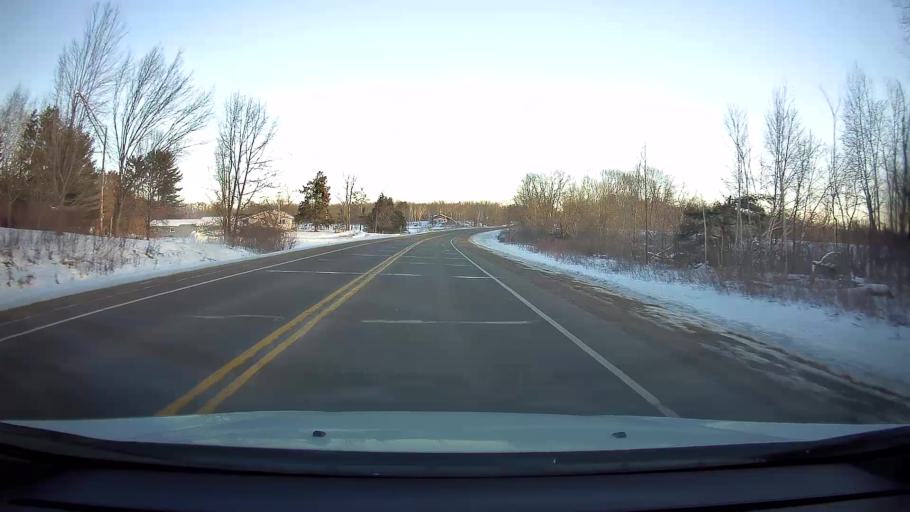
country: US
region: Wisconsin
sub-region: Barron County
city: Turtle Lake
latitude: 45.4066
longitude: -92.1390
